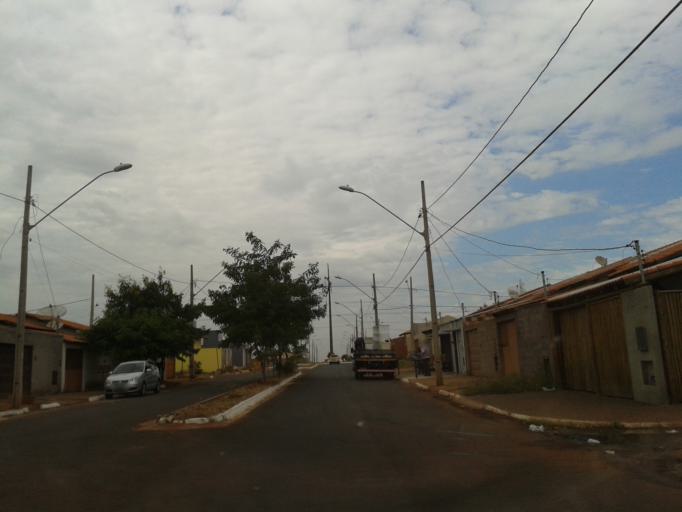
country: BR
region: Minas Gerais
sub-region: Santa Vitoria
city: Santa Vitoria
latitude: -18.8567
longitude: -50.1238
